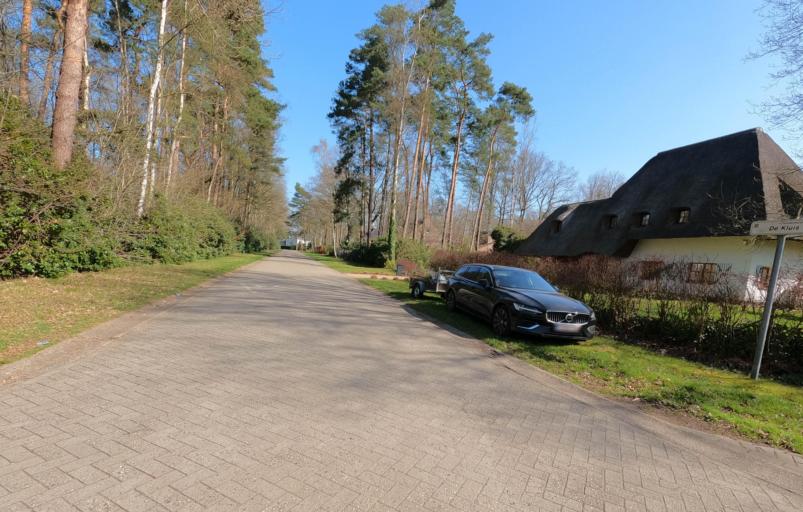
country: BE
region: Flanders
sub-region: Provincie Antwerpen
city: Schilde
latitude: 51.2412
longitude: 4.5638
